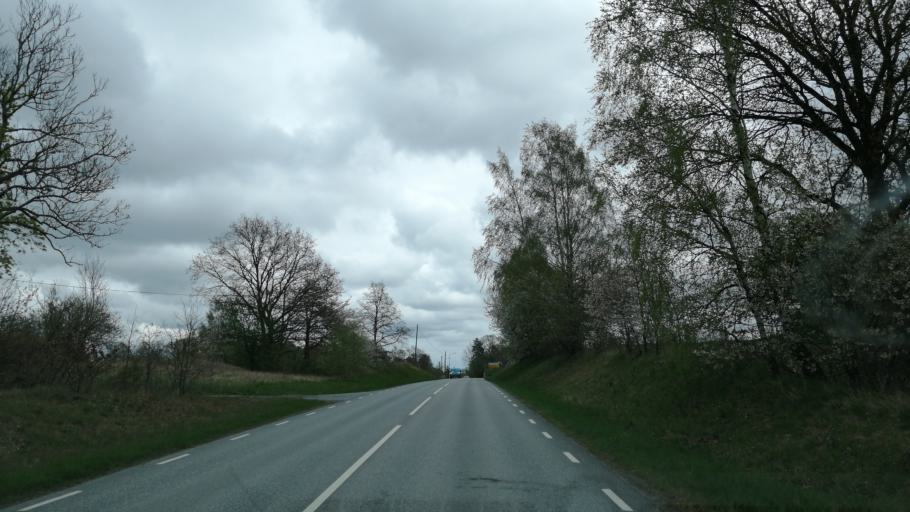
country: SE
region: Skane
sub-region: Kristianstads Kommun
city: Onnestad
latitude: 55.9948
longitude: 14.0617
